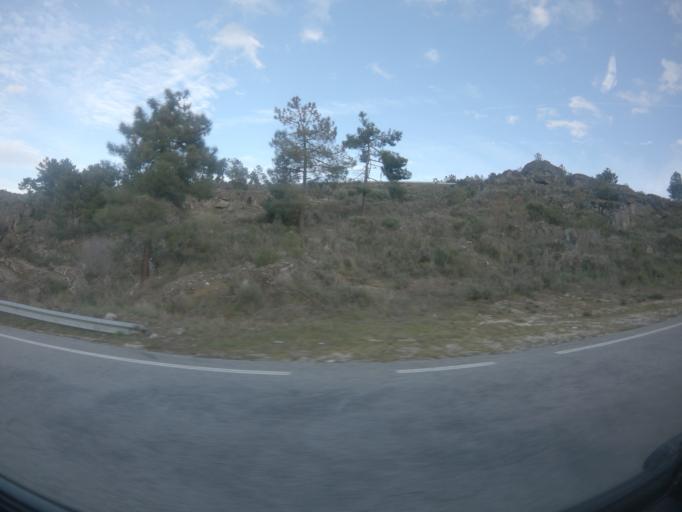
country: PT
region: Braganca
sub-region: Carrazeda de Ansiaes
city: Carrazeda de Anciaes
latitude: 41.2847
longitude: -7.3374
